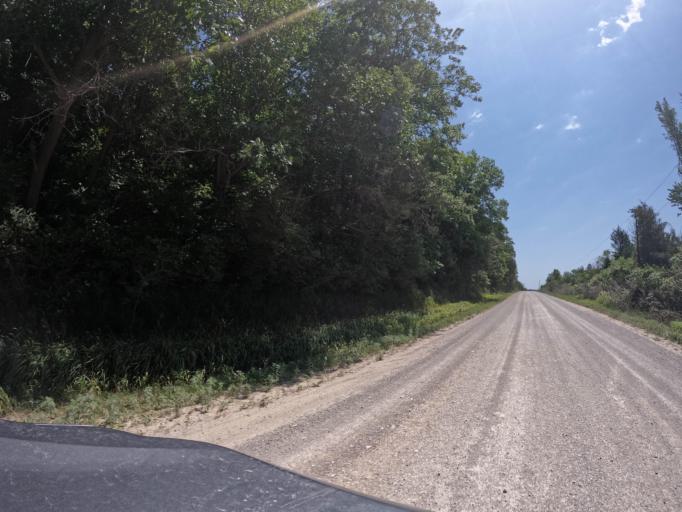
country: US
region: Iowa
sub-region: Henry County
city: Mount Pleasant
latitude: 40.8941
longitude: -91.5471
